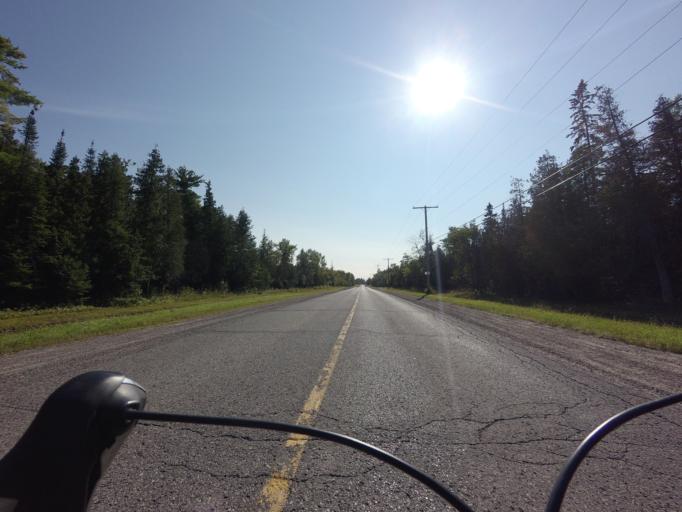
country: CA
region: Ontario
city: Bells Corners
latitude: 45.4730
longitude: -75.9983
